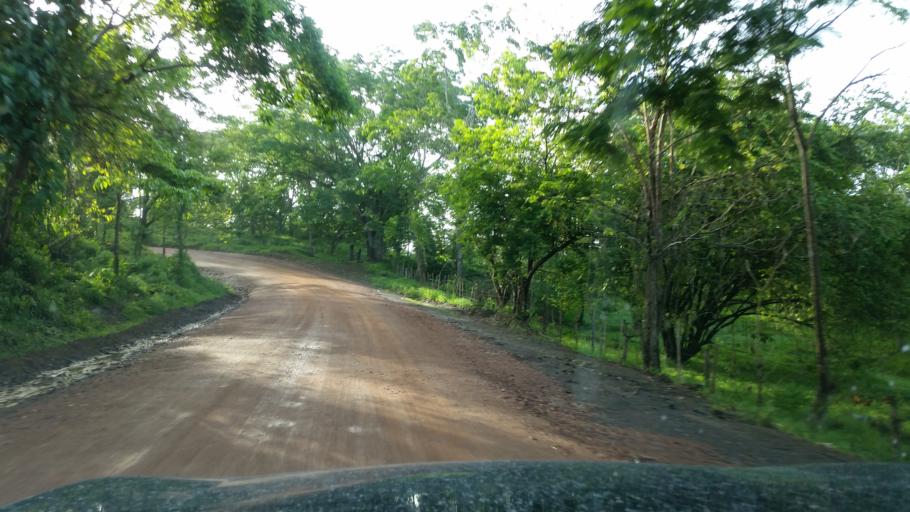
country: NI
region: Atlantico Norte (RAAN)
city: Puerto Cabezas
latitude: 14.0672
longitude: -83.9727
